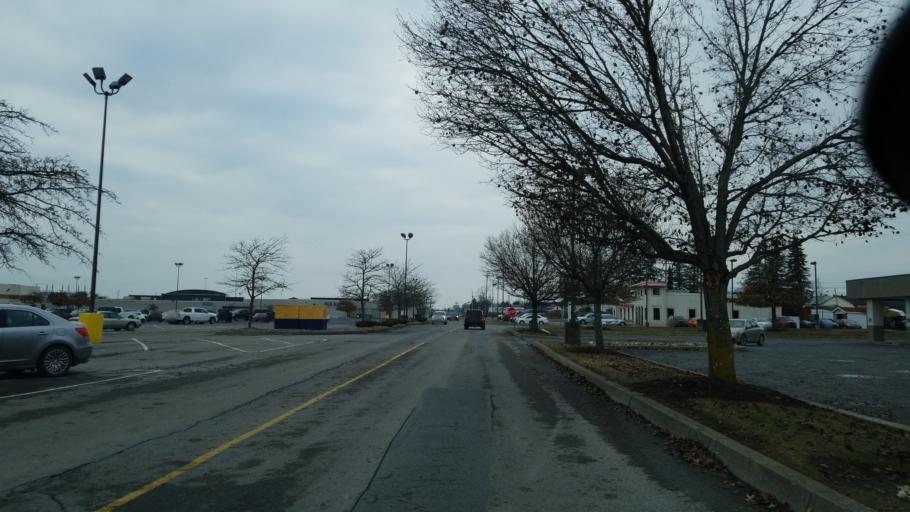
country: US
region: Pennsylvania
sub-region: Clearfield County
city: DuBois
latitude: 41.1211
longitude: -78.7239
